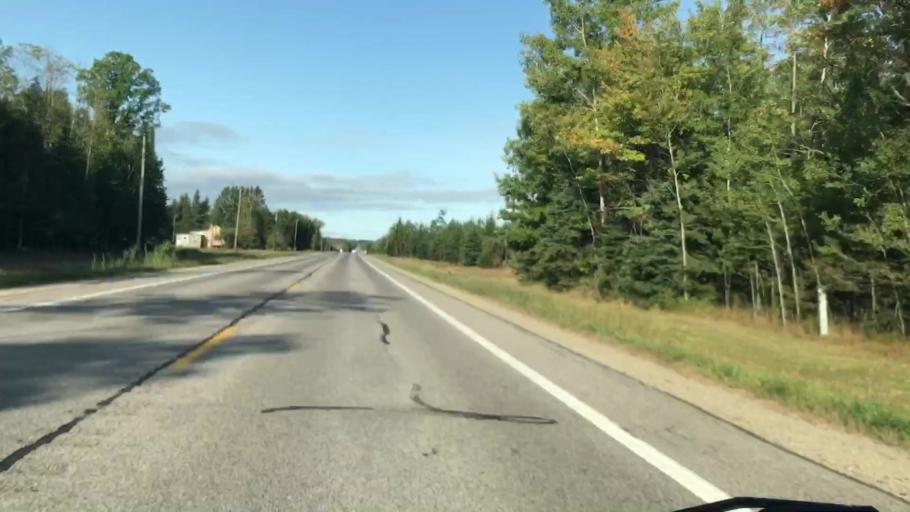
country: US
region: Michigan
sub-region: Luce County
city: Newberry
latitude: 46.3034
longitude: -85.3705
